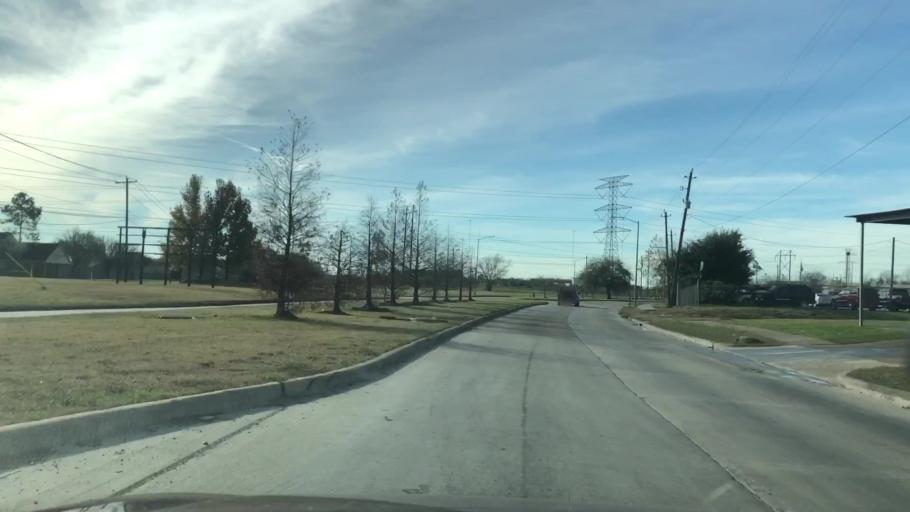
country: US
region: Texas
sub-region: Fort Bend County
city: Missouri City
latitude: 29.6317
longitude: -95.4933
